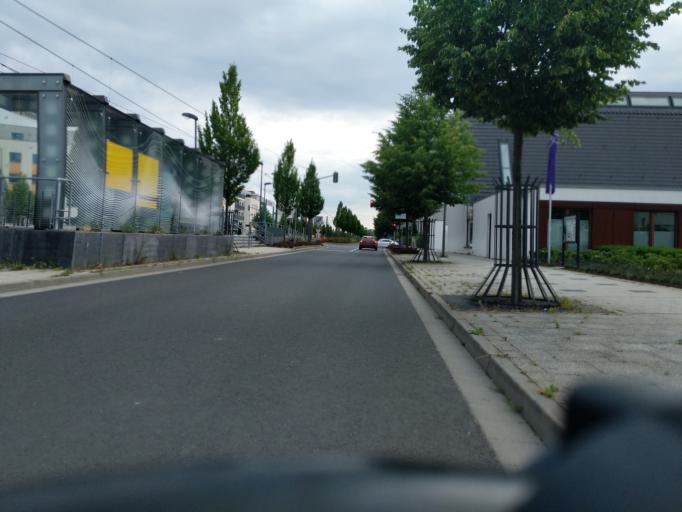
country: DE
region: Hesse
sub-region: Regierungsbezirk Darmstadt
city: Bad Homburg vor der Hoehe
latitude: 50.1797
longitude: 8.6352
